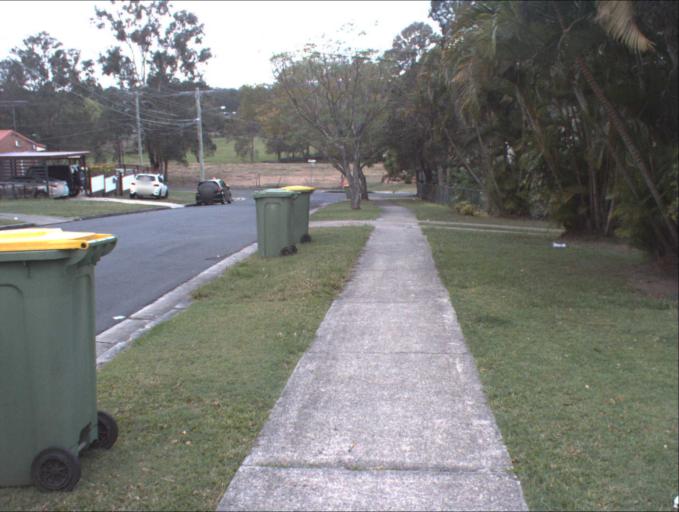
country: AU
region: Queensland
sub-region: Logan
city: Waterford West
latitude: -27.6807
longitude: 153.1341
